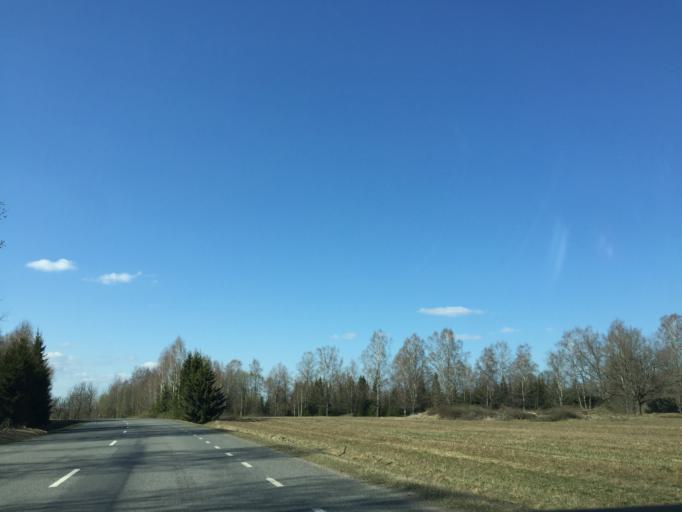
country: EE
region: Viljandimaa
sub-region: Viiratsi vald
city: Viiratsi
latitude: 58.2714
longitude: 25.6155
